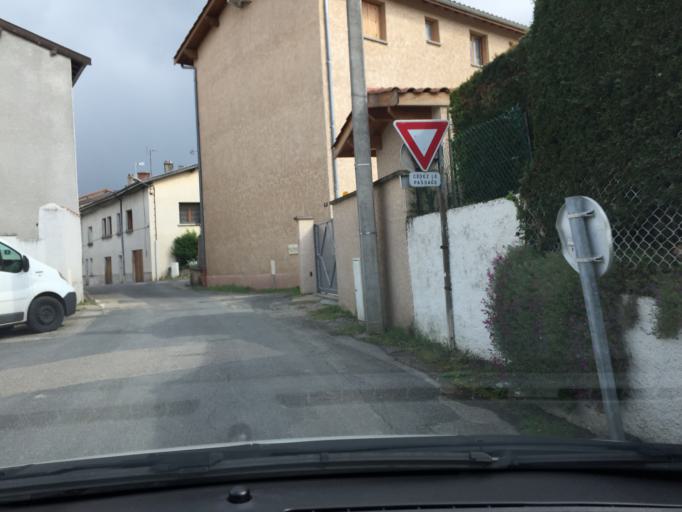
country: FR
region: Rhone-Alpes
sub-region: Departement du Rhone
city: Orlienas
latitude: 45.6589
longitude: 4.7175
